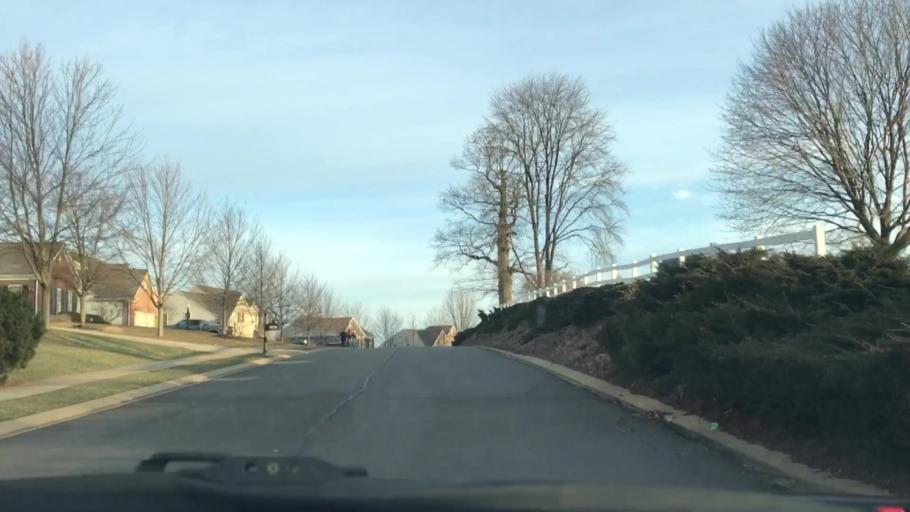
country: US
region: Pennsylvania
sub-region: Allegheny County
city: Franklin Park
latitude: 40.5868
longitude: -80.0902
